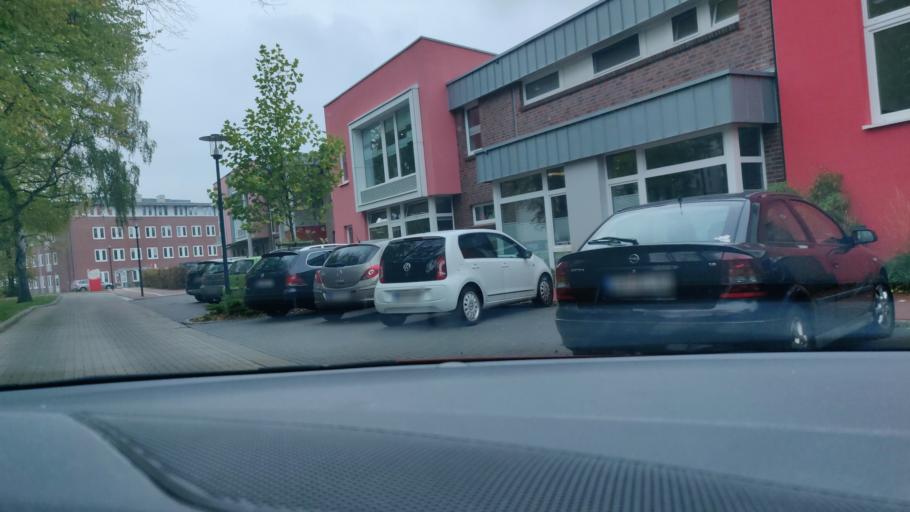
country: DE
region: Lower Saxony
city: Cuxhaven
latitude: 53.8690
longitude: 8.6959
